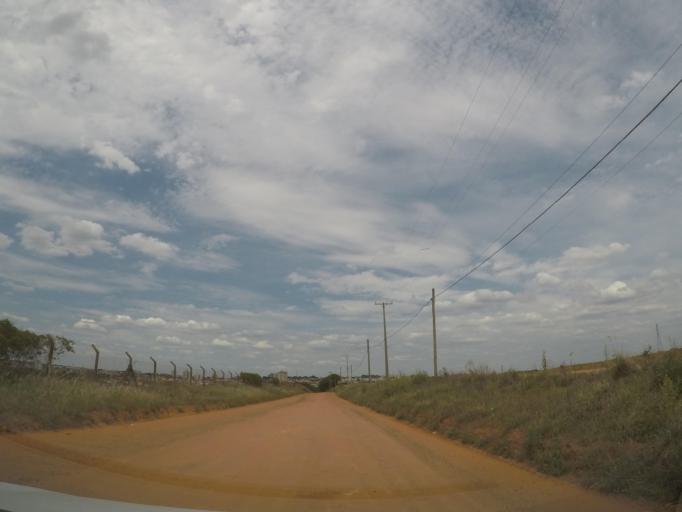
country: BR
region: Sao Paulo
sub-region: Sumare
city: Sumare
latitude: -22.8347
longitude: -47.2896
